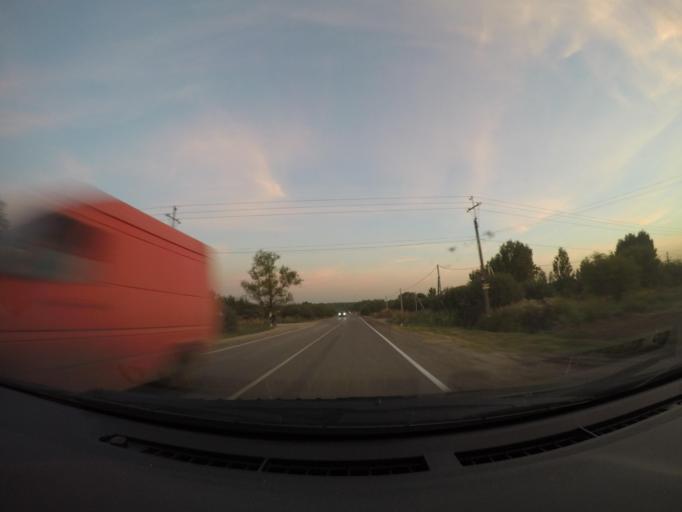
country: RU
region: Moskovskaya
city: Rechitsy
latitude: 55.5957
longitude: 38.4334
